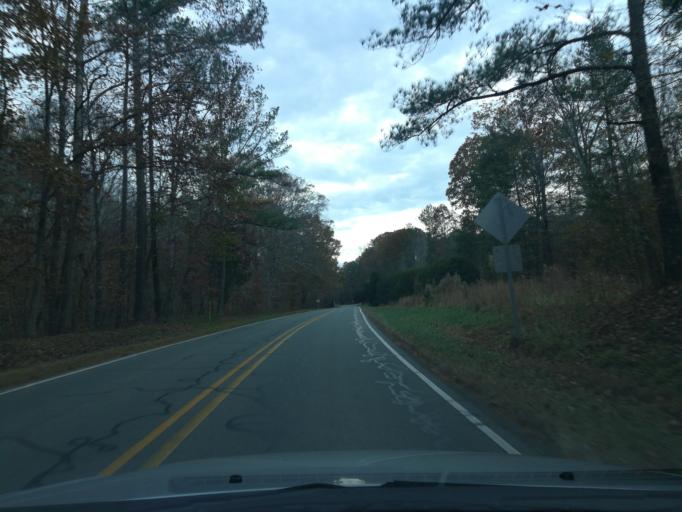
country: US
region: North Carolina
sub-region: Orange County
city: Chapel Hill
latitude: 35.9953
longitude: -79.0552
